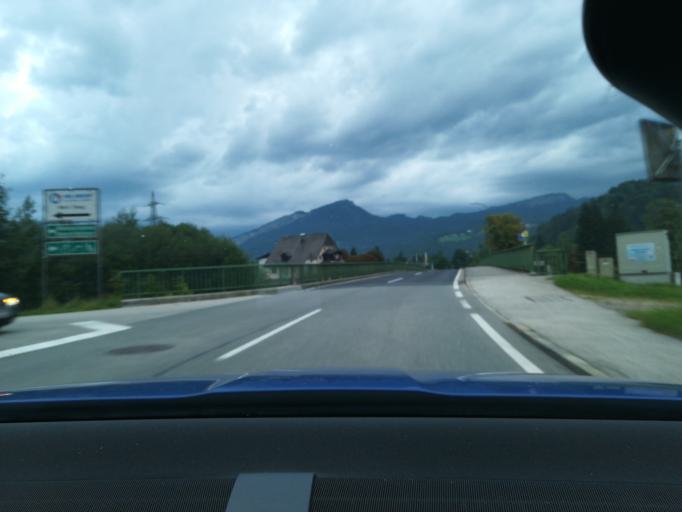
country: AT
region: Upper Austria
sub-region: Politischer Bezirk Gmunden
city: Bad Goisern
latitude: 47.6106
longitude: 13.6322
